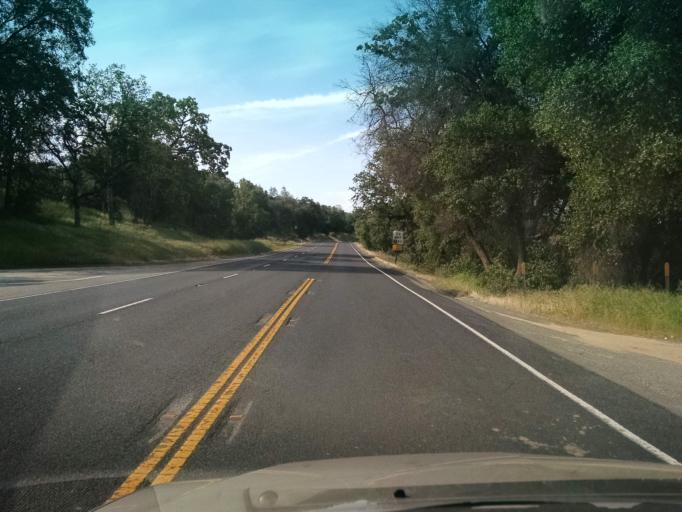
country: US
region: California
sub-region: Madera County
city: Coarsegold
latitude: 37.2375
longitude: -119.7070
